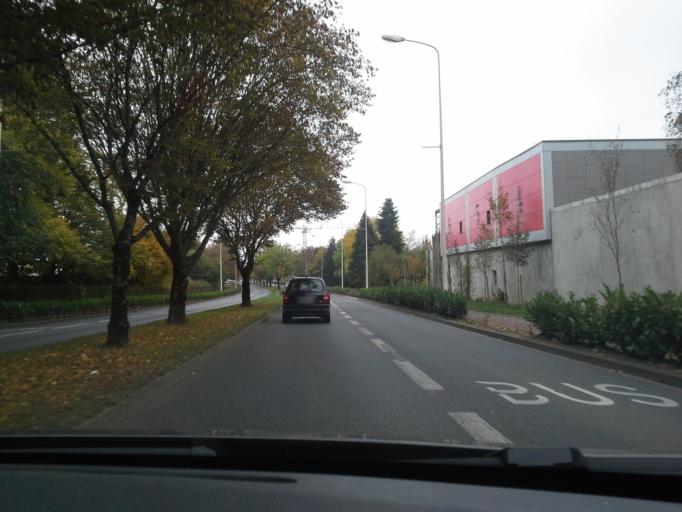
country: FR
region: Centre
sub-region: Departement d'Indre-et-Loire
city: Tours
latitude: 47.4169
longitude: 0.7038
